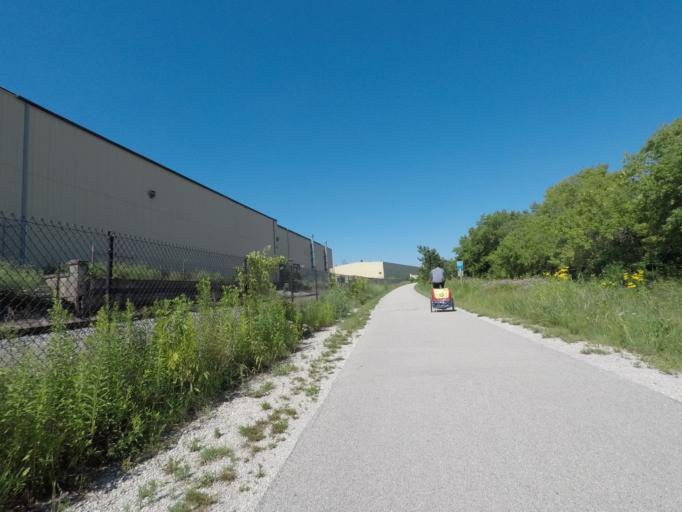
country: US
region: Wisconsin
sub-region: Milwaukee County
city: West Milwaukee
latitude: 43.0241
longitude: -87.9634
